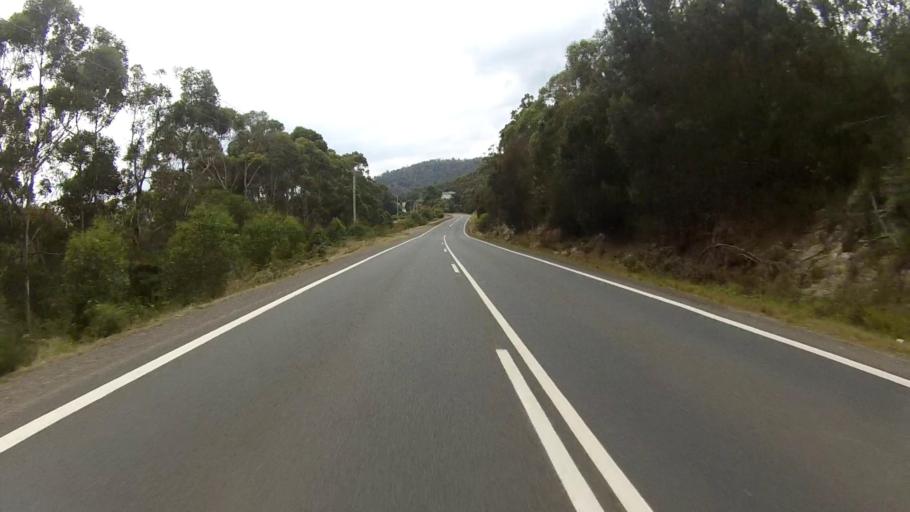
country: AU
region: Tasmania
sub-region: Huon Valley
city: Huonville
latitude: -43.0579
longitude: 147.0445
